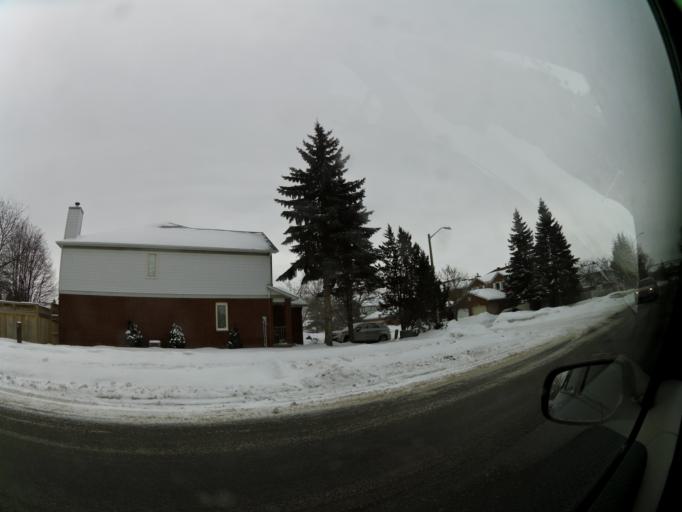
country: CA
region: Ontario
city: Ottawa
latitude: 45.3690
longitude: -75.6157
